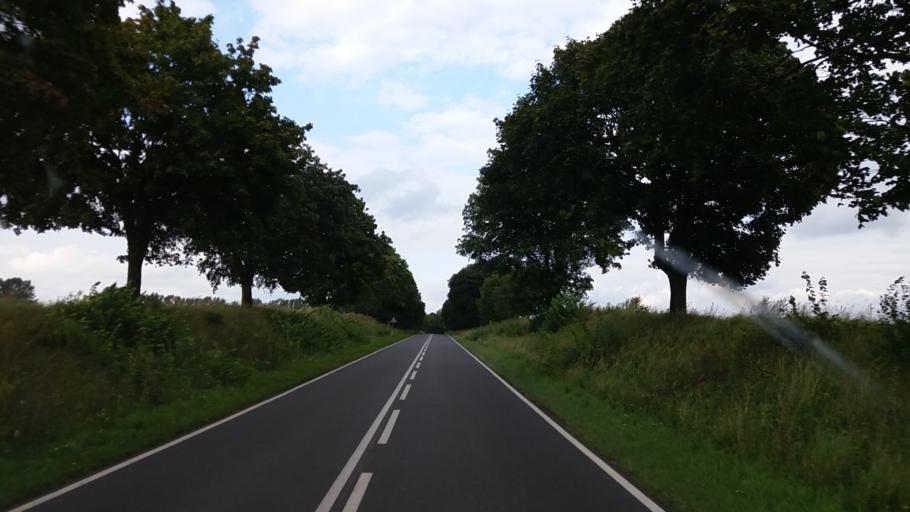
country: PL
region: West Pomeranian Voivodeship
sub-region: Powiat choszczenski
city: Choszczno
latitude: 53.1503
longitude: 15.3813
